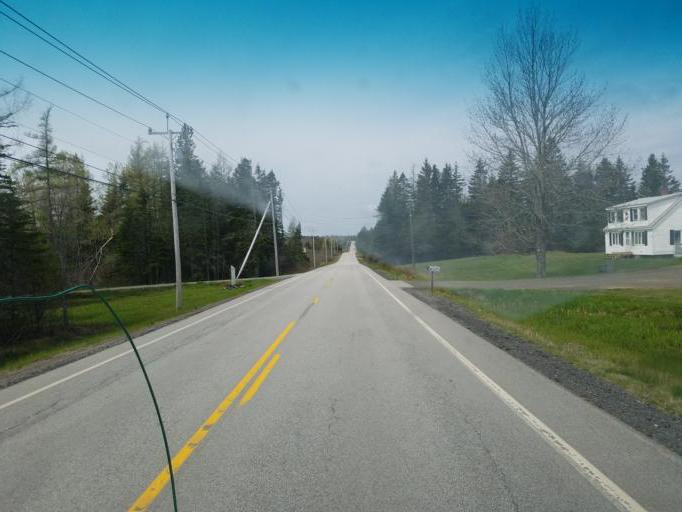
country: US
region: Maine
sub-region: Washington County
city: Eastport
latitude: 44.8035
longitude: -67.1100
